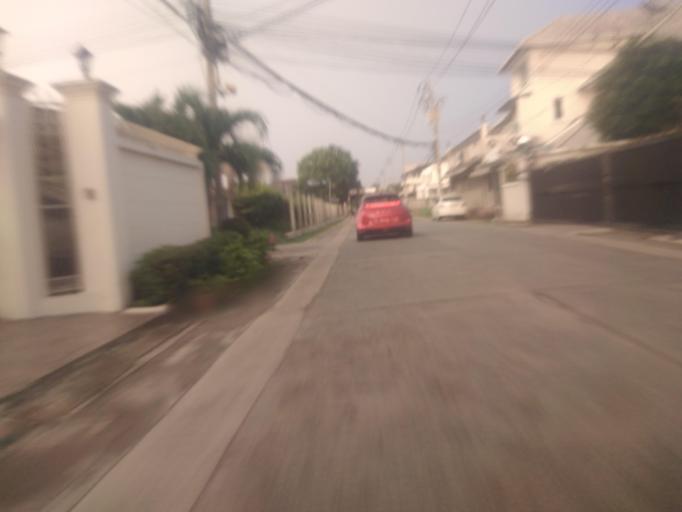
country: TH
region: Bangkok
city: Phasi Charoen
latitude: 13.7424
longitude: 100.4435
